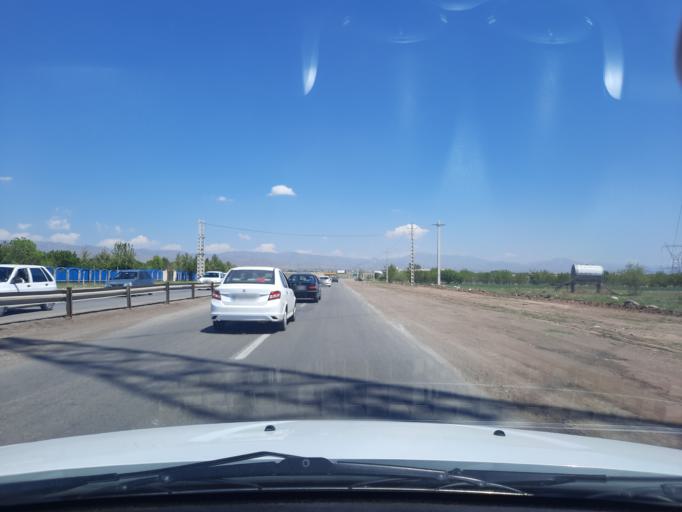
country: IR
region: Qazvin
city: Qazvin
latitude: 36.2684
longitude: 50.0853
